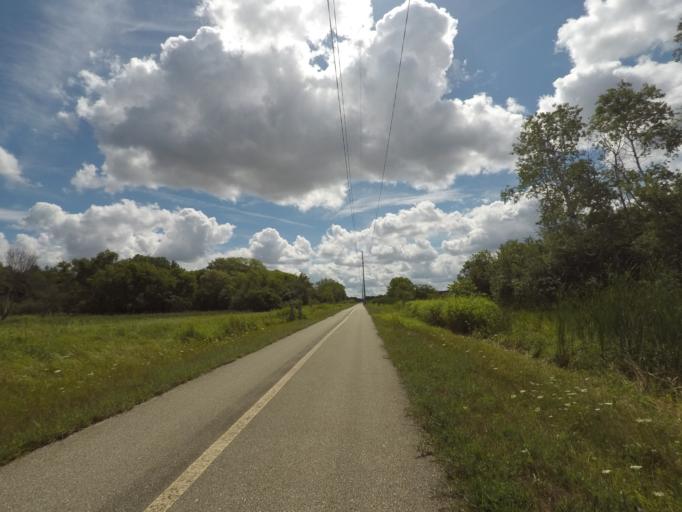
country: US
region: Wisconsin
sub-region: Waukesha County
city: Pewaukee
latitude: 43.0576
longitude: -88.2930
